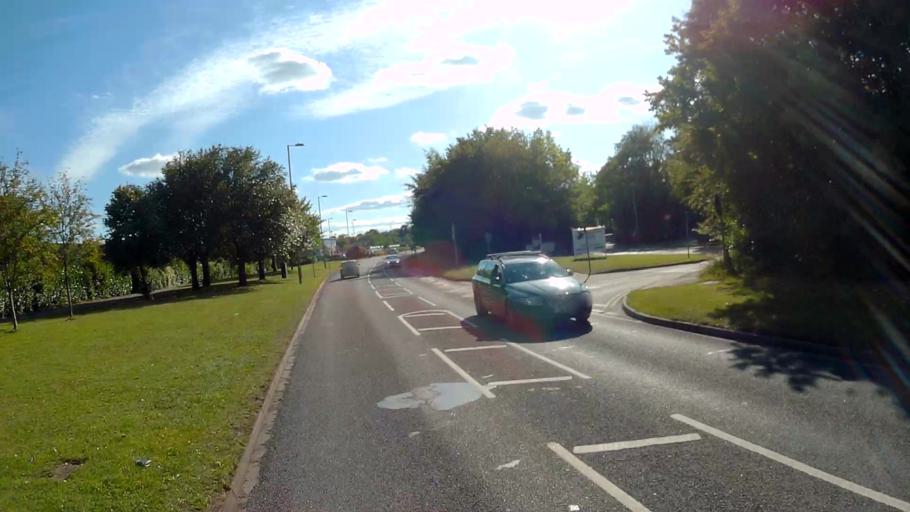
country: GB
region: England
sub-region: Hampshire
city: Basingstoke
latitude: 51.2471
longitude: -1.1128
